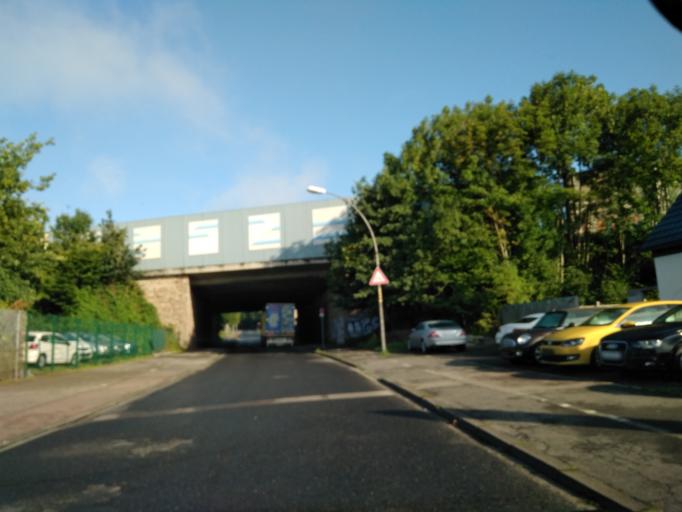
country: DE
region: North Rhine-Westphalia
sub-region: Regierungsbezirk Munster
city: Gelsenkirchen
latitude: 51.5640
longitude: 7.0762
